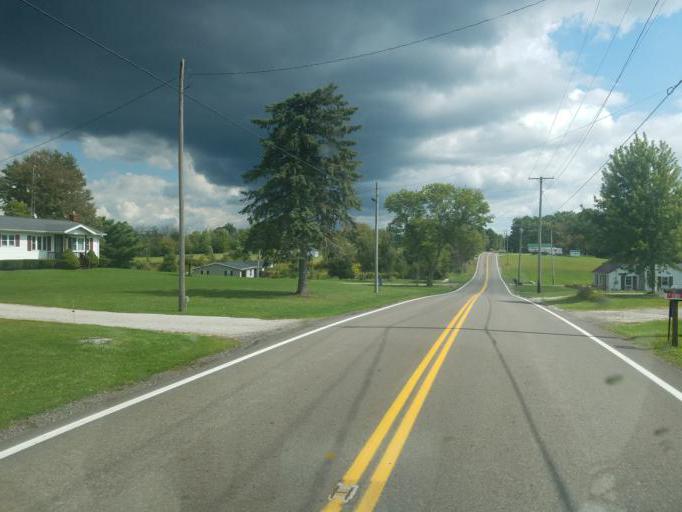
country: US
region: Ohio
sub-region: Huron County
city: Greenwich
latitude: 40.9259
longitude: -82.5289
